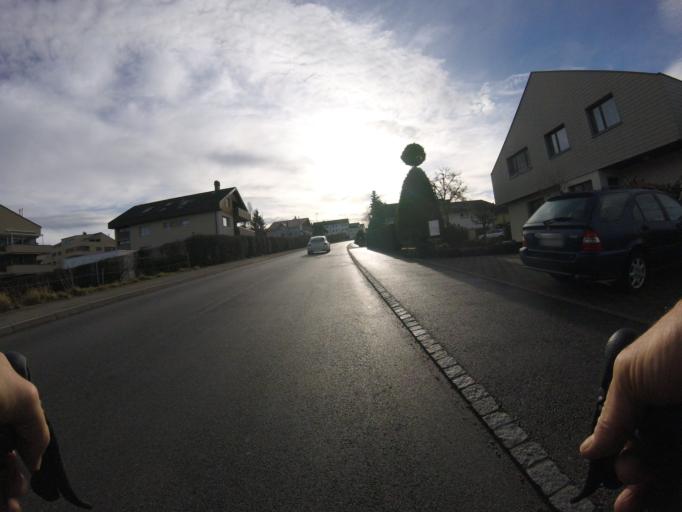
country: CH
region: Fribourg
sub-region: Sense District
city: Ueberstorf
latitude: 46.8640
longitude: 7.3118
